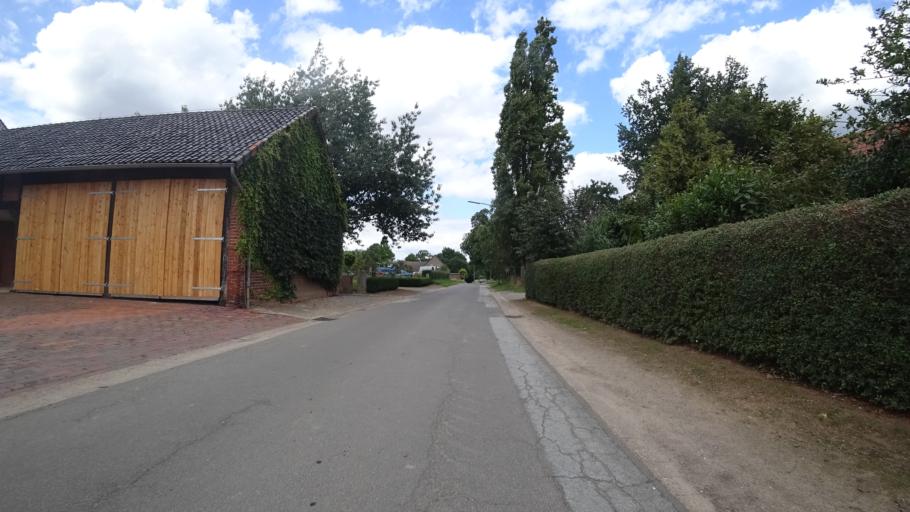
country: DE
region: North Rhine-Westphalia
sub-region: Regierungsbezirk Detmold
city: Petershagen
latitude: 52.4111
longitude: 9.0058
